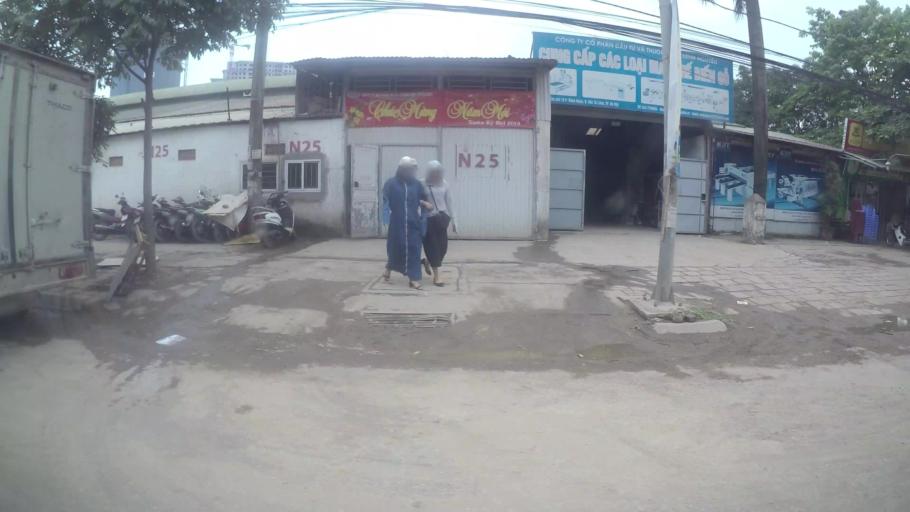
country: VN
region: Ha Noi
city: Tay Ho
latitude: 21.0836
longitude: 105.7856
